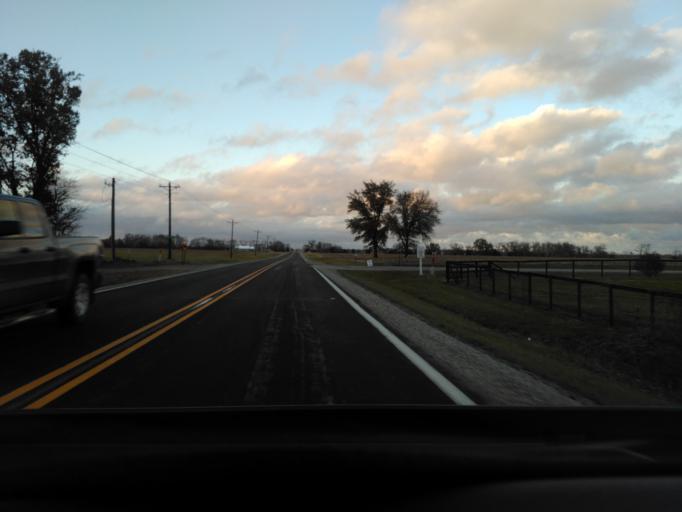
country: US
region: Illinois
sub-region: Effingham County
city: Altamont
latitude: 38.9859
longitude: -88.7488
